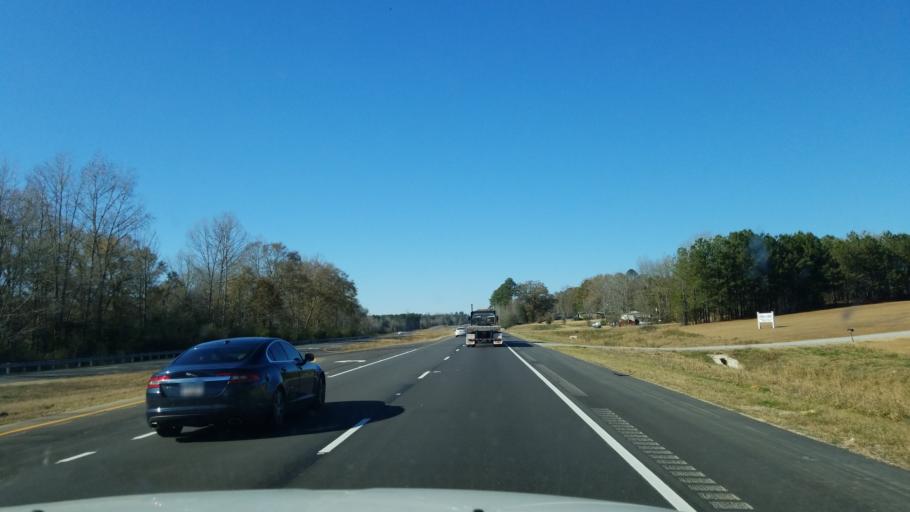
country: US
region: Alabama
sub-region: Pickens County
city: Gordo
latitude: 33.3484
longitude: -87.9531
